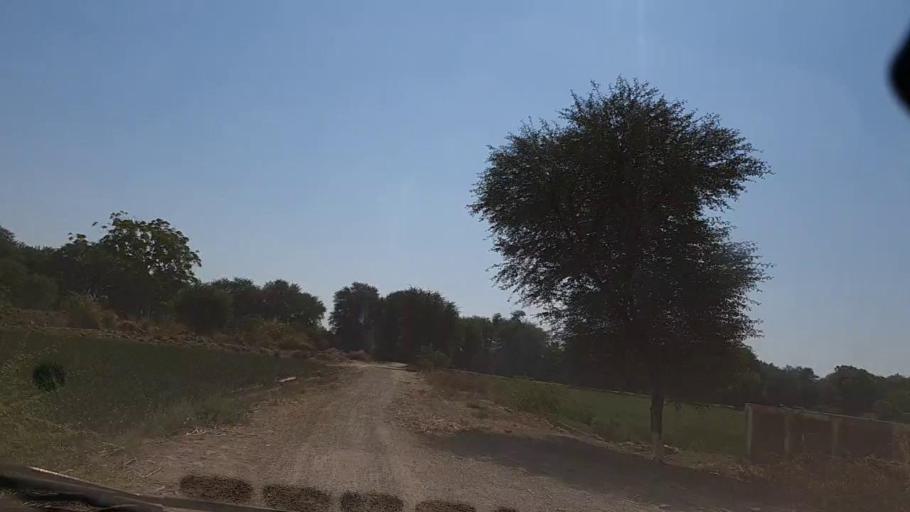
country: PK
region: Sindh
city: Mirpur Khas
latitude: 25.4269
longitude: 69.0559
